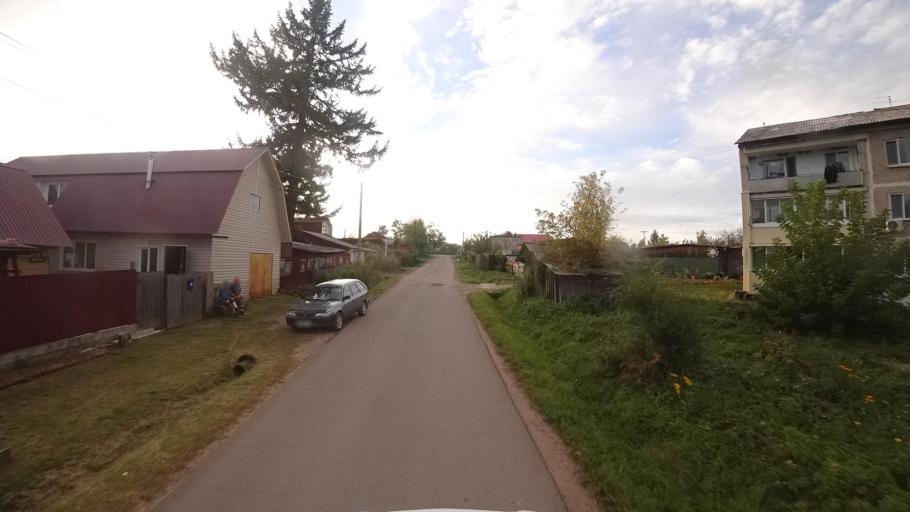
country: RU
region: Primorskiy
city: Yakovlevka
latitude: 44.4218
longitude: 133.4731
